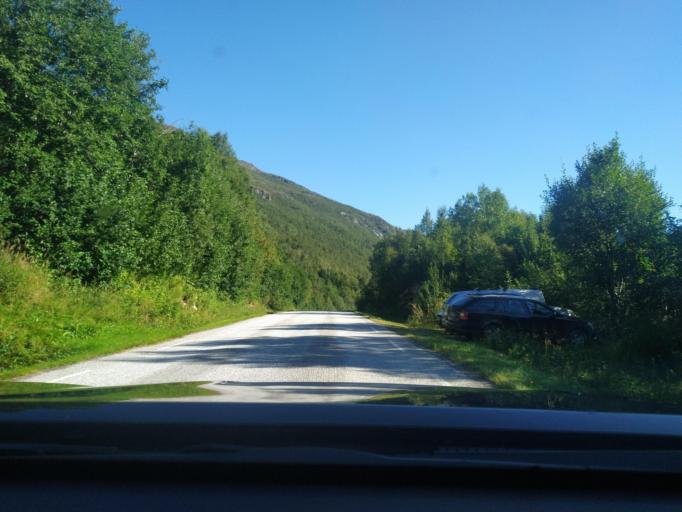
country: NO
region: Troms
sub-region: Dyroy
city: Brostadbotn
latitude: 68.9274
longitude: 17.6428
